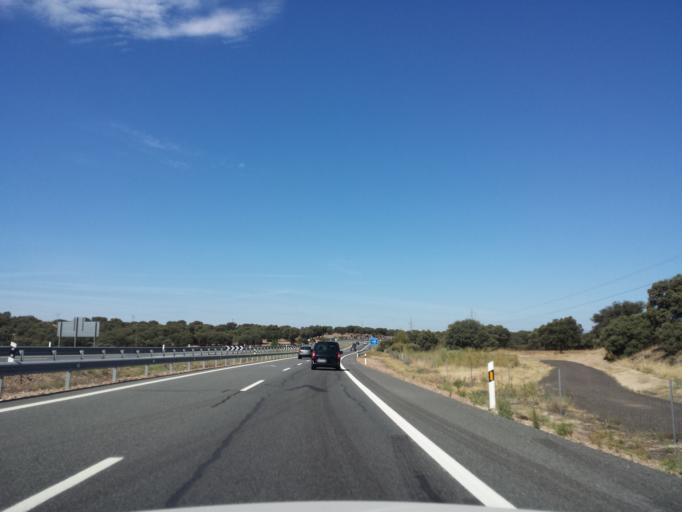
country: ES
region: Castille-La Mancha
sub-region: Province of Toledo
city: Alcanizo
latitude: 39.9169
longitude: -5.0694
